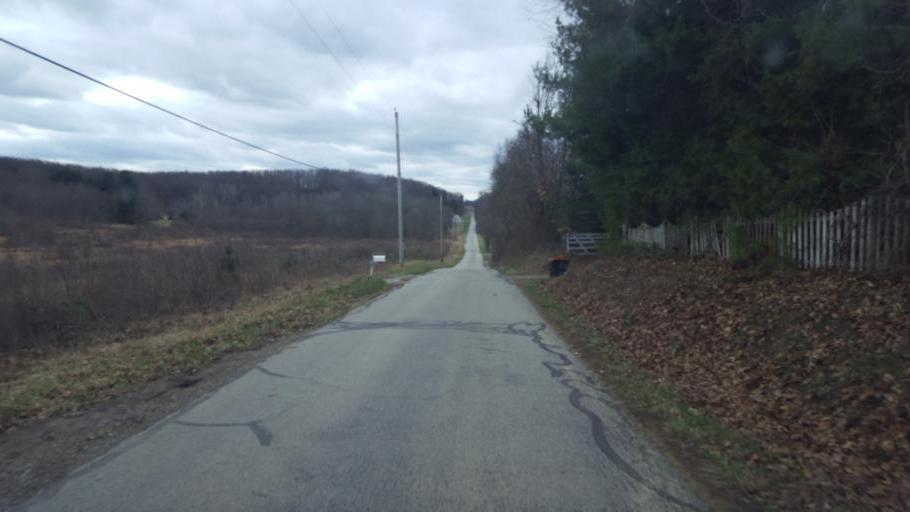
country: US
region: Ohio
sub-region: Licking County
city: Utica
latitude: 40.2051
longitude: -82.3911
